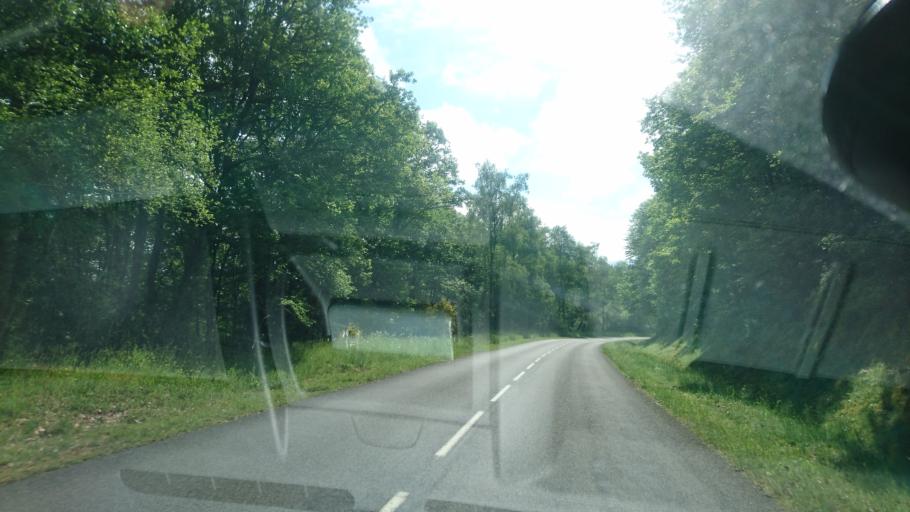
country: FR
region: Limousin
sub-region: Departement de la Haute-Vienne
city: Peyrat-le-Chateau
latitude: 45.7954
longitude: 1.8471
